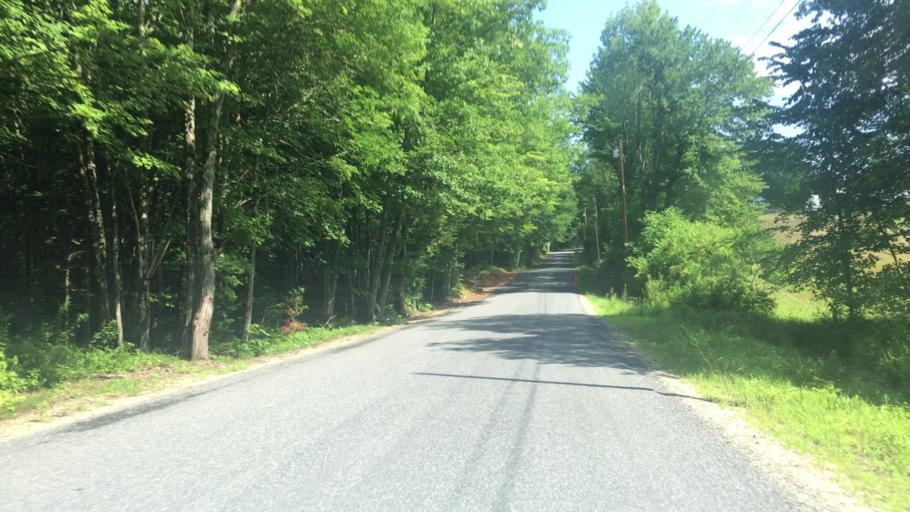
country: US
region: Maine
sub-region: Oxford County
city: Paris
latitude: 44.2930
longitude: -70.5251
